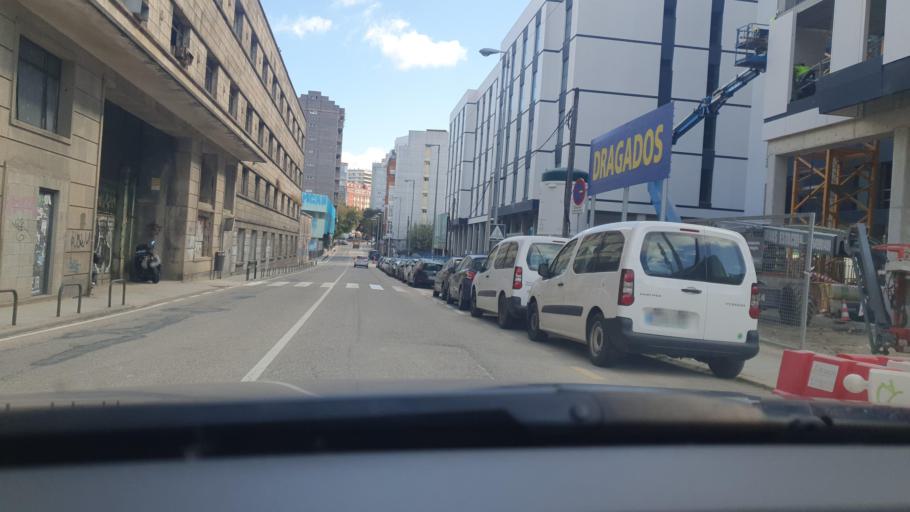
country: ES
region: Galicia
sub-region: Provincia de Pontevedra
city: Vigo
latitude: 42.2238
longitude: -8.7390
